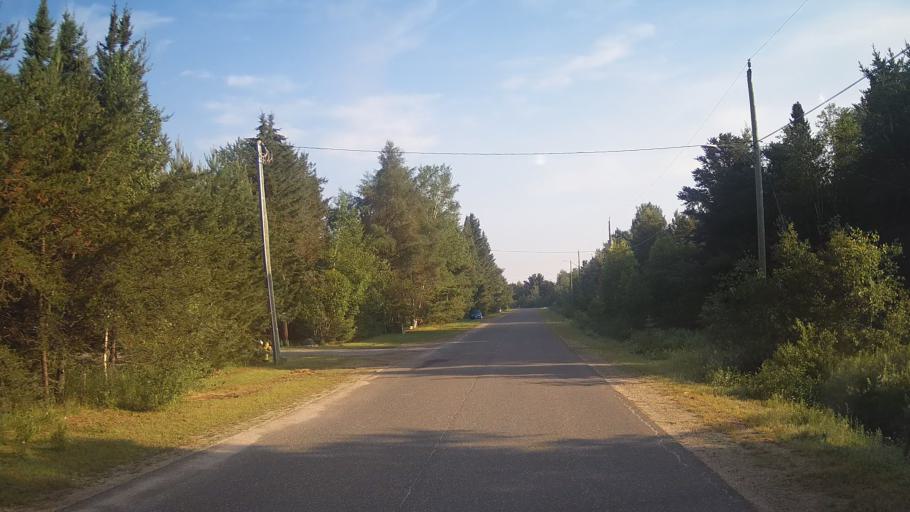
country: CA
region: Ontario
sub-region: Rainy River District
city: Atikokan
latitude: 49.4020
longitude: -91.6656
